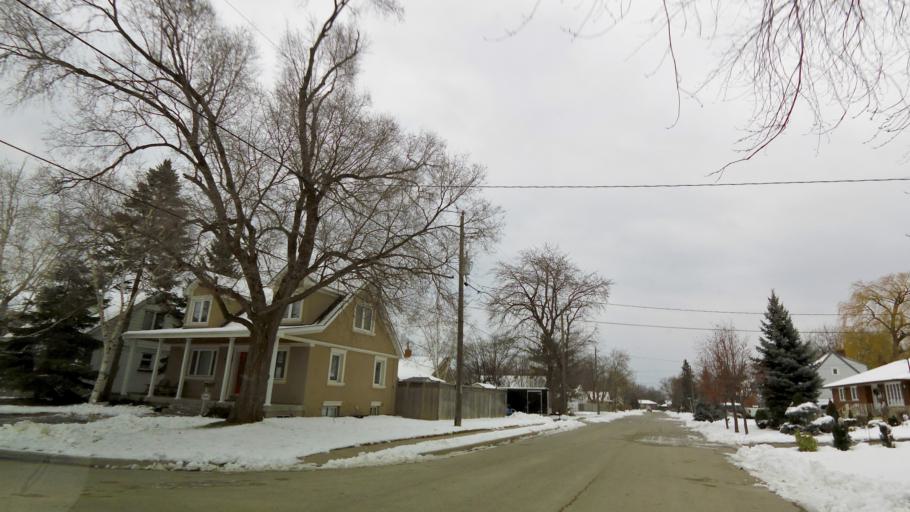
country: CA
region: Ontario
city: Etobicoke
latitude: 43.5802
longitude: -79.5659
